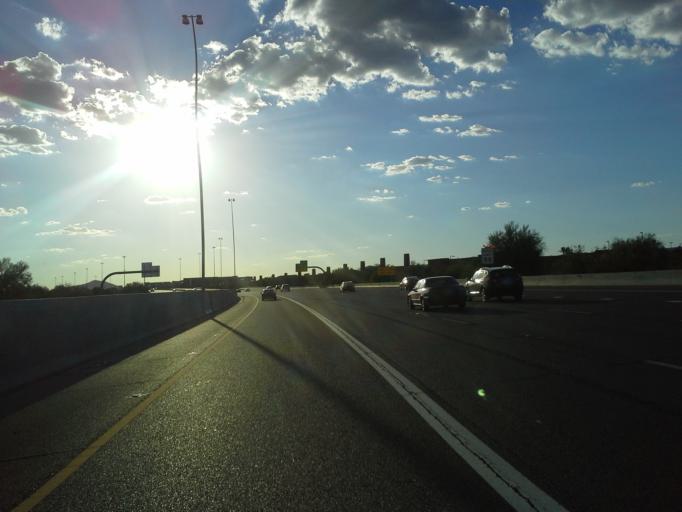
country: US
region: Arizona
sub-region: Maricopa County
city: Paradise Valley
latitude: 33.6718
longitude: -111.9683
